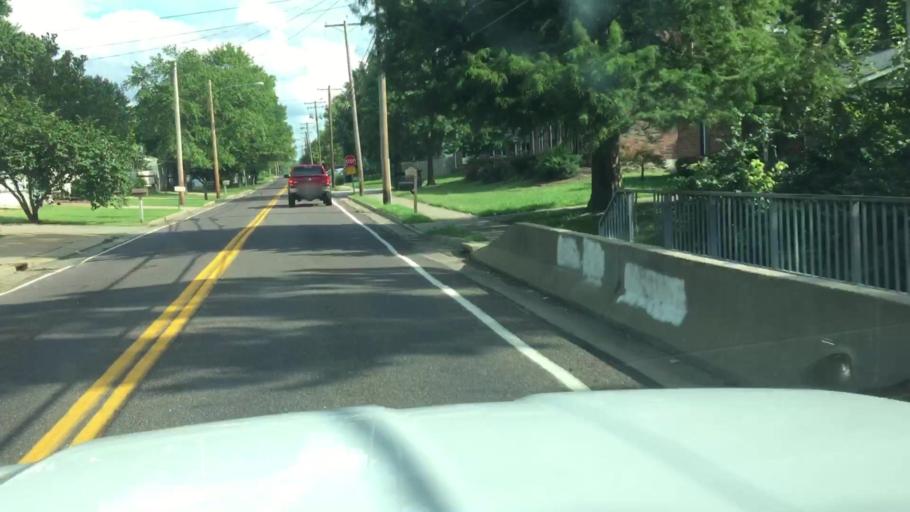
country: US
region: Missouri
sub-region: Jefferson County
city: Arnold
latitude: 38.4491
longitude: -90.3580
